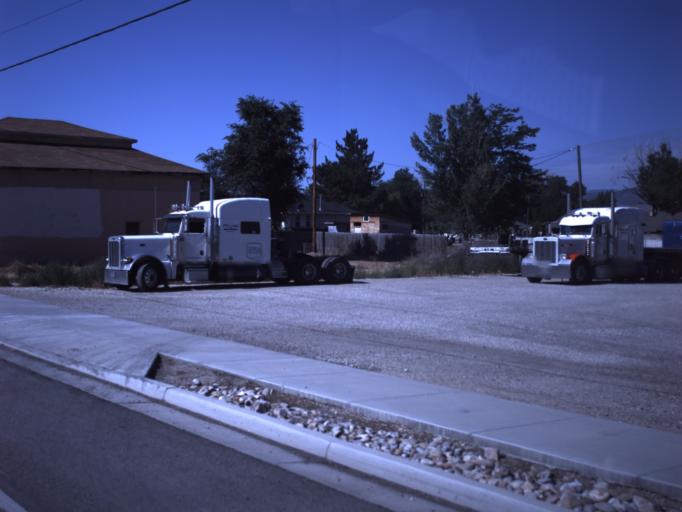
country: US
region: Utah
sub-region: Sanpete County
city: Centerfield
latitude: 39.1257
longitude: -111.8193
